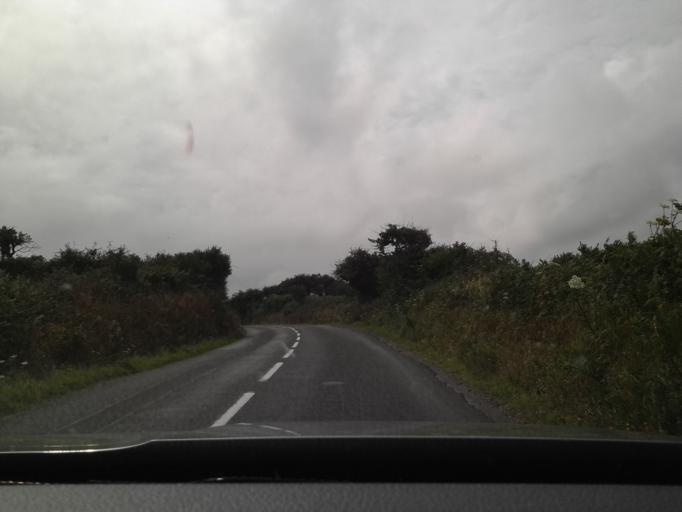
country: FR
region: Lower Normandy
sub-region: Departement de la Manche
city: Urville-Nacqueville
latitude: 49.6784
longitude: -1.7749
